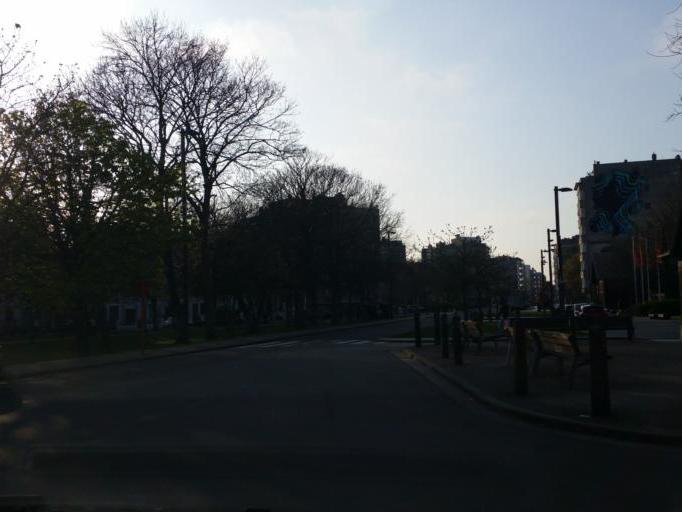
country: BE
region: Flanders
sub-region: Provincie West-Vlaanderen
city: Ostend
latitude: 51.2225
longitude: 2.9122
